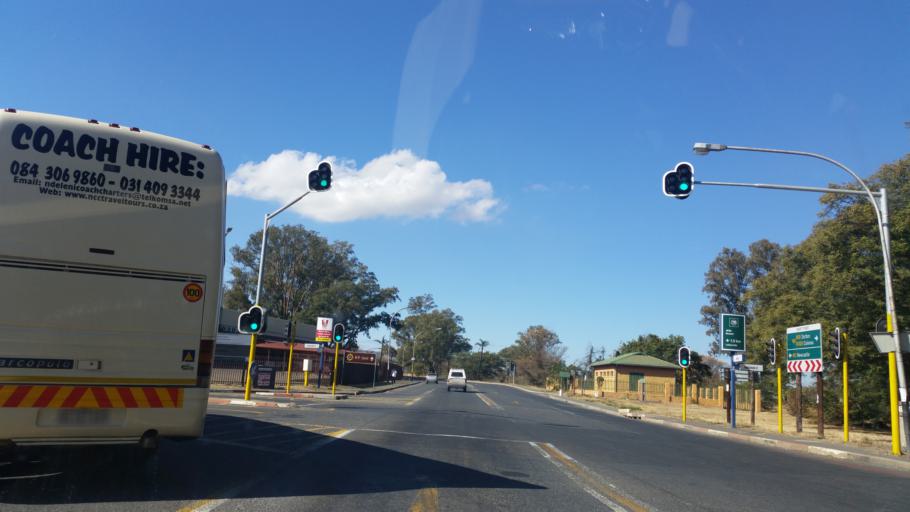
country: ZA
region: KwaZulu-Natal
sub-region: uThukela District Municipality
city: Ladysmith
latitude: -28.5687
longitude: 29.7738
